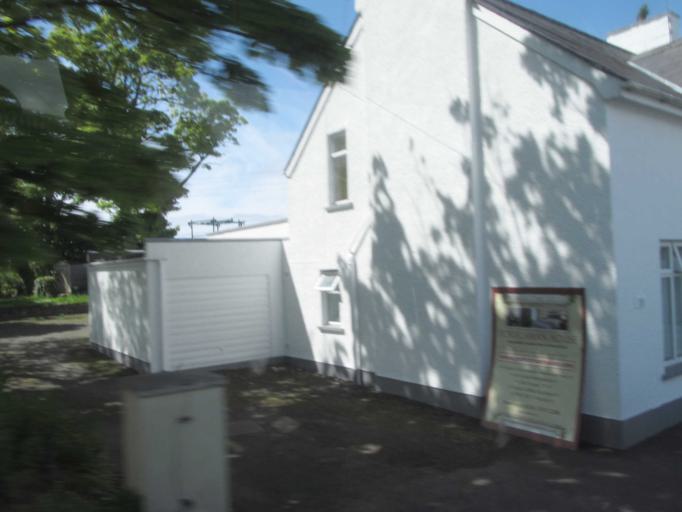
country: GB
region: Northern Ireland
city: Bushmills
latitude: 55.2035
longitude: -6.5260
